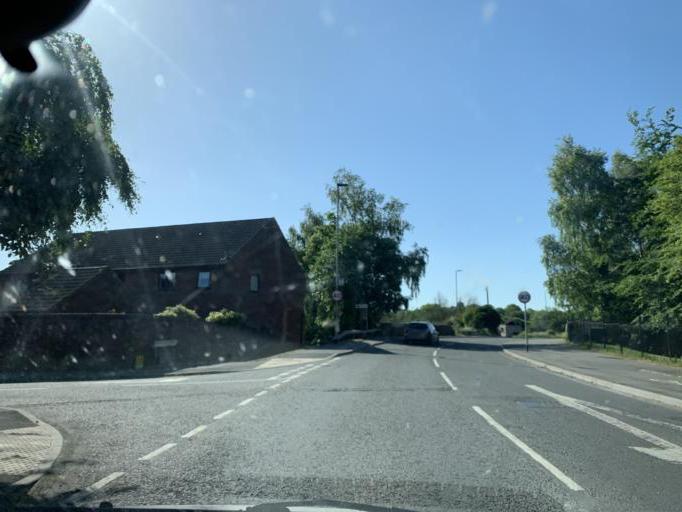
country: GB
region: England
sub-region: Wiltshire
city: Devizes
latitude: 51.3605
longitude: -1.9754
